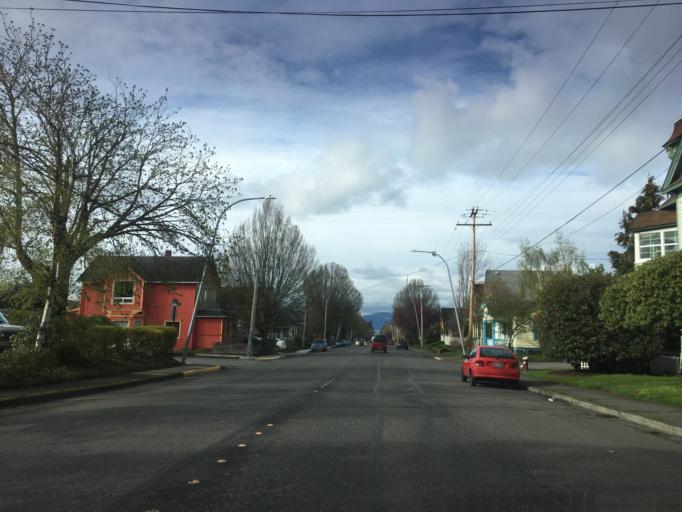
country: US
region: Washington
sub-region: Whatcom County
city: Bellingham
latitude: 48.7624
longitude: -122.4769
